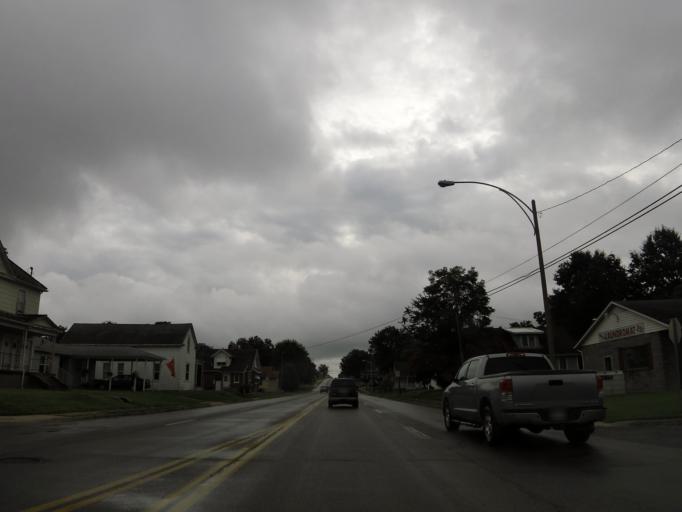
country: US
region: Missouri
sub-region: Cape Girardeau County
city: Cape Girardeau
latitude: 37.3018
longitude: -89.5357
